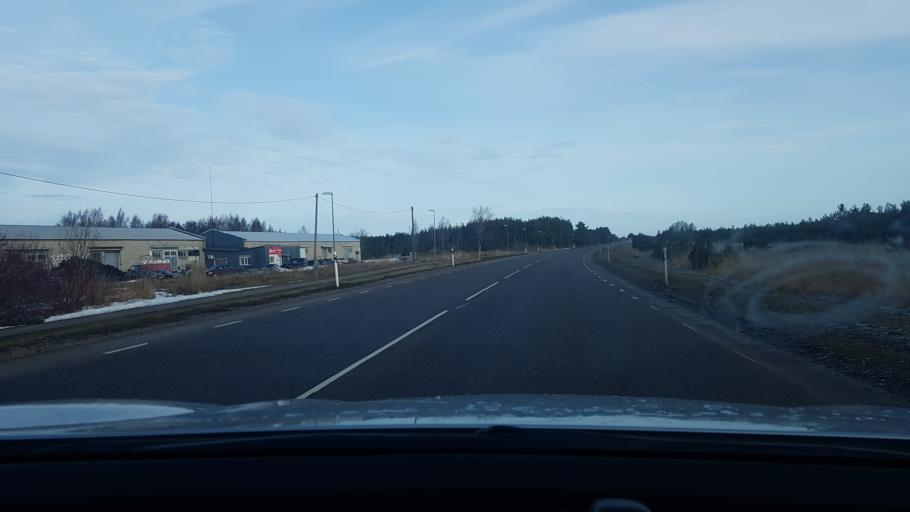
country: EE
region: Saare
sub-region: Kuressaare linn
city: Kuressaare
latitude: 58.2373
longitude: 22.5004
